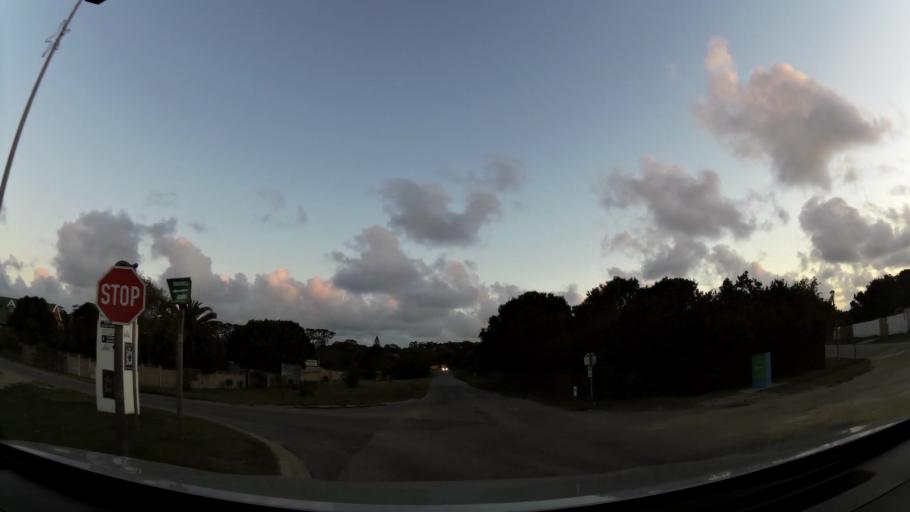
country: ZA
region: Western Cape
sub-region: Eden District Municipality
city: Knysna
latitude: -34.0261
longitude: 22.8073
